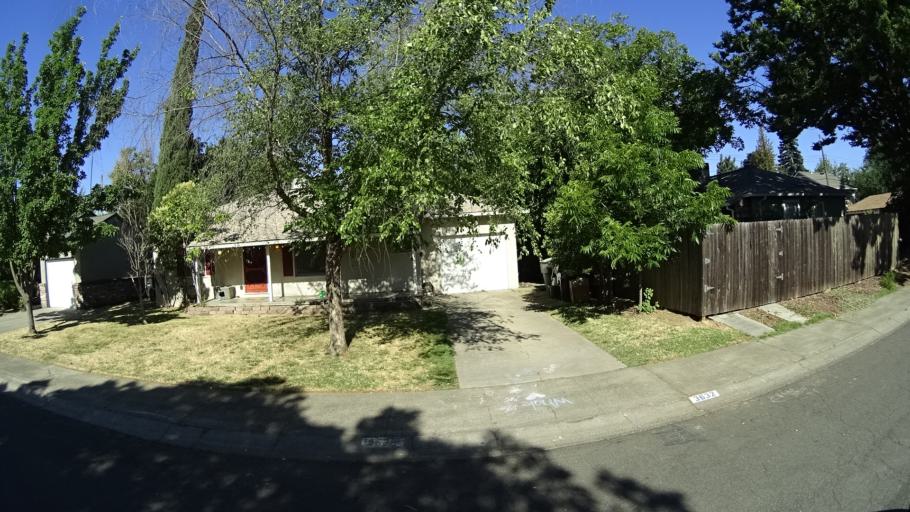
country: US
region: California
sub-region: Sacramento County
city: Parkway
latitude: 38.5419
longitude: -121.4414
